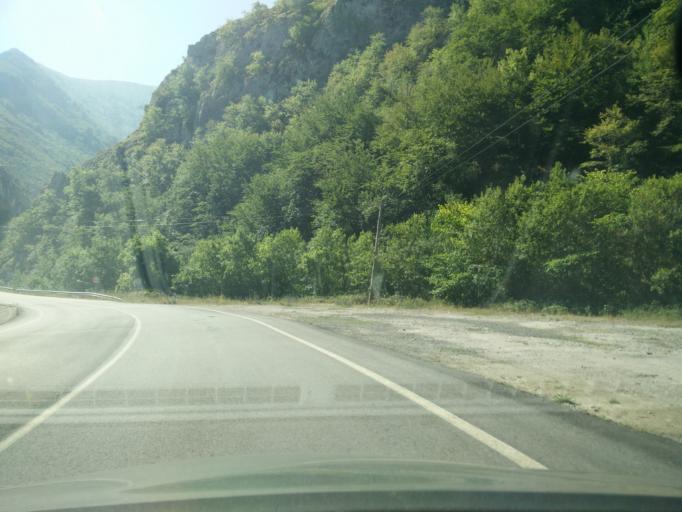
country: ES
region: Asturias
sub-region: Province of Asturias
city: Campo de Caso
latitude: 43.1807
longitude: -5.3631
